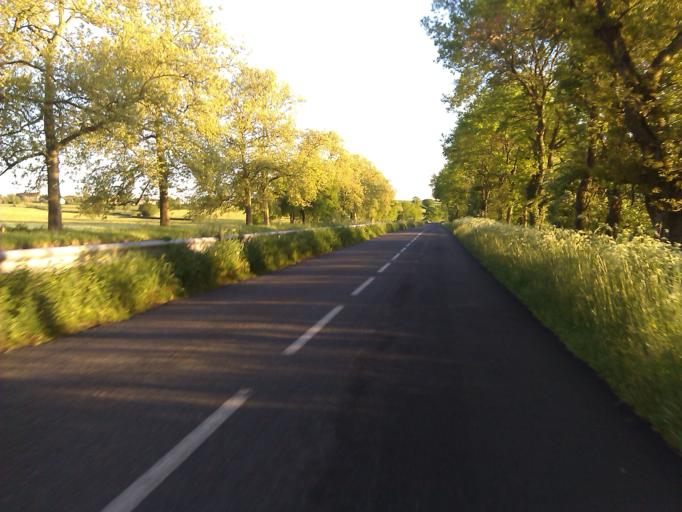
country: FR
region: Bourgogne
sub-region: Departement de Saone-et-Loire
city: Palinges
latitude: 46.5133
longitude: 4.1945
